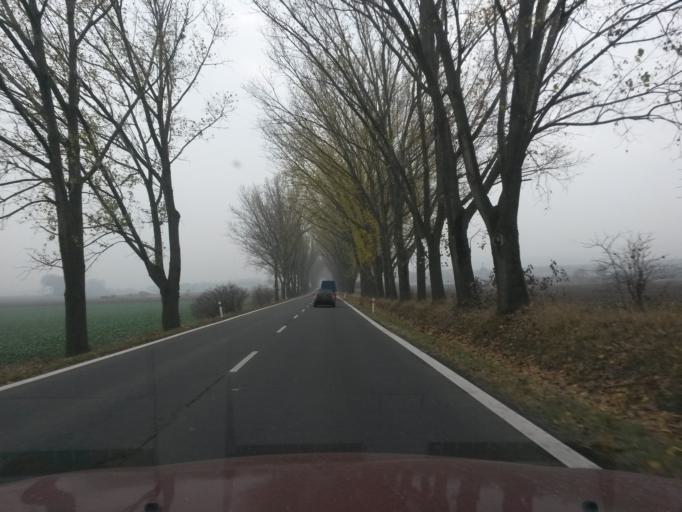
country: SK
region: Kosicky
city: Kosice
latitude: 48.8132
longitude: 21.3002
